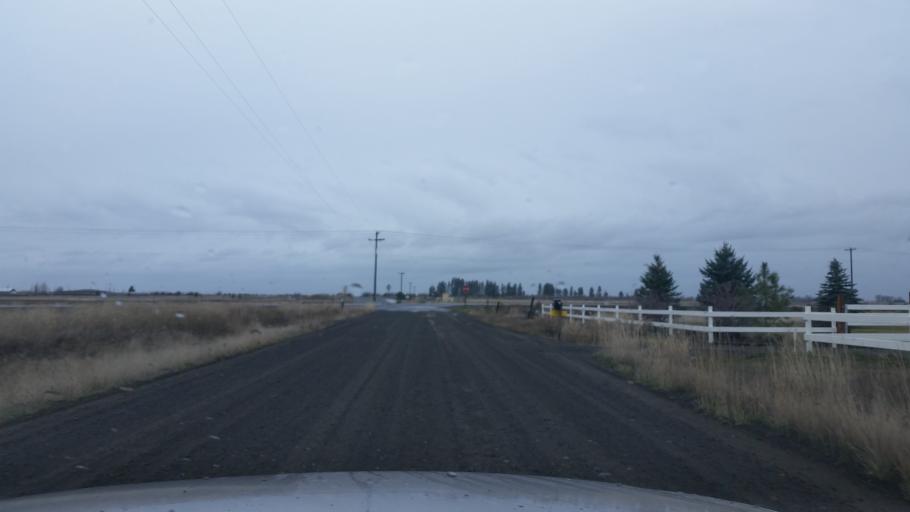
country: US
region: Washington
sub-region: Spokane County
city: Fairchild Air Force Base
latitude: 47.5900
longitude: -117.6289
